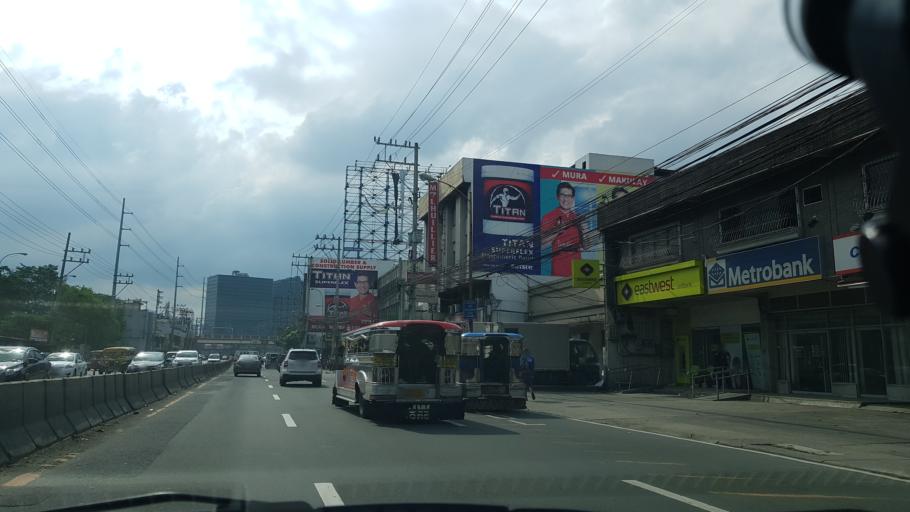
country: PH
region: Metro Manila
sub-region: Pasig
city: Pasig City
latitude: 14.5904
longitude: 121.0890
